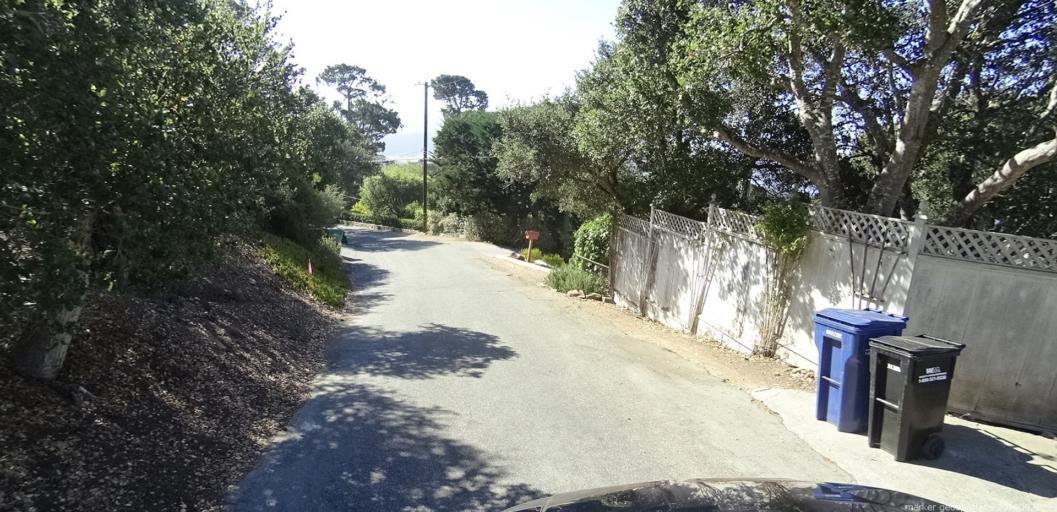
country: US
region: California
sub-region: Monterey County
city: Carmel-by-the-Sea
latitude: 36.5634
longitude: -121.9139
